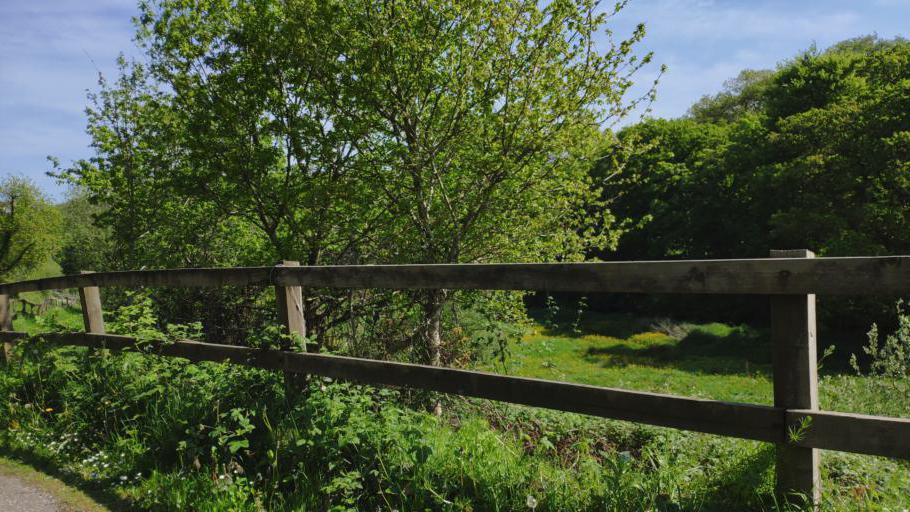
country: IE
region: Munster
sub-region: County Cork
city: Blarney
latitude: 51.9381
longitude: -8.5639
